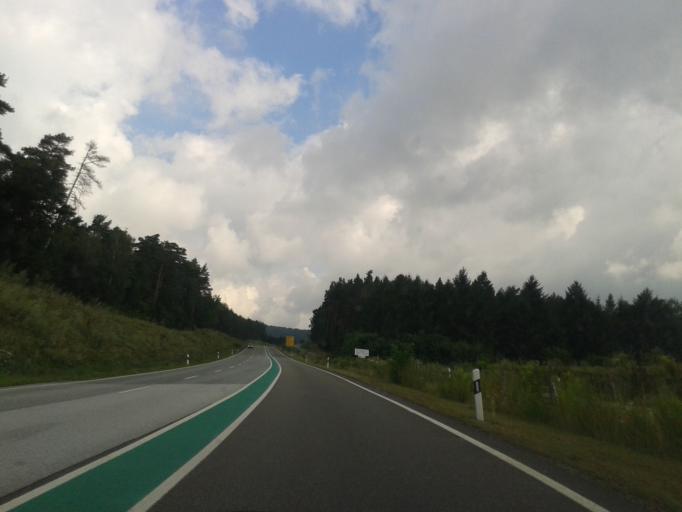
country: DE
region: Saxony
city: Pirna
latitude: 50.9928
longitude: 13.9374
